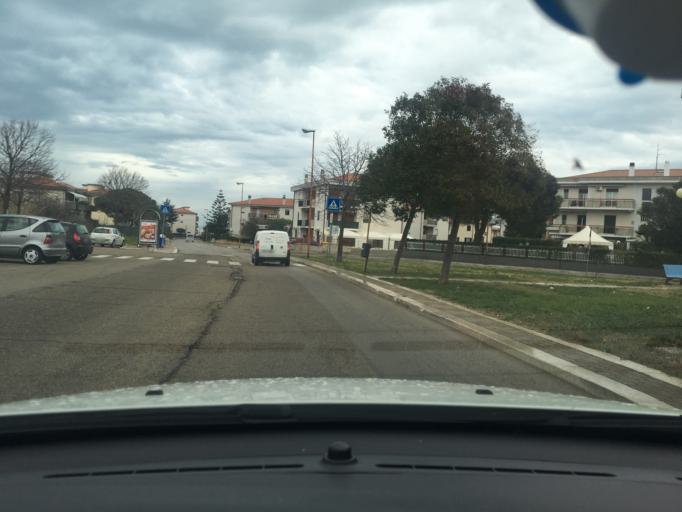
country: IT
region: Molise
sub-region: Provincia di Campobasso
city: Termoli
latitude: 41.9726
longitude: 14.9938
